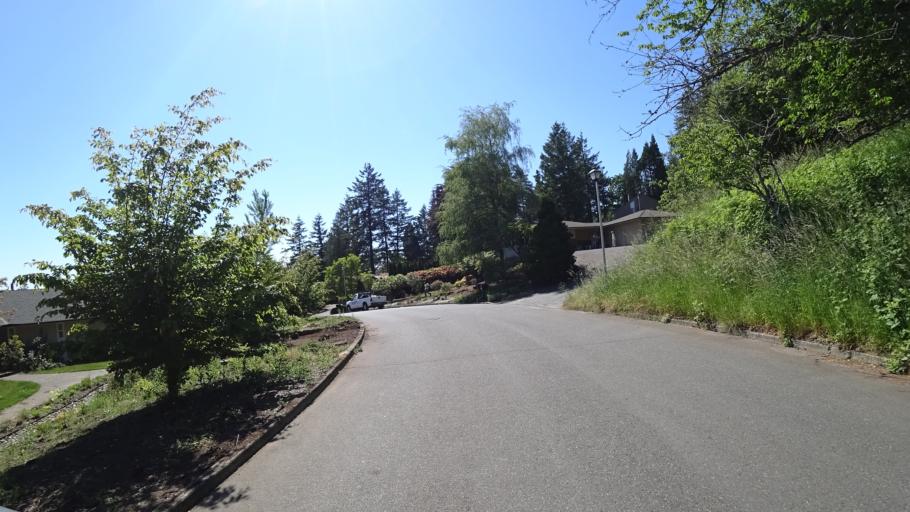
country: US
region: Oregon
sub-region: Washington County
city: West Slope
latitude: 45.4982
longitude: -122.7196
